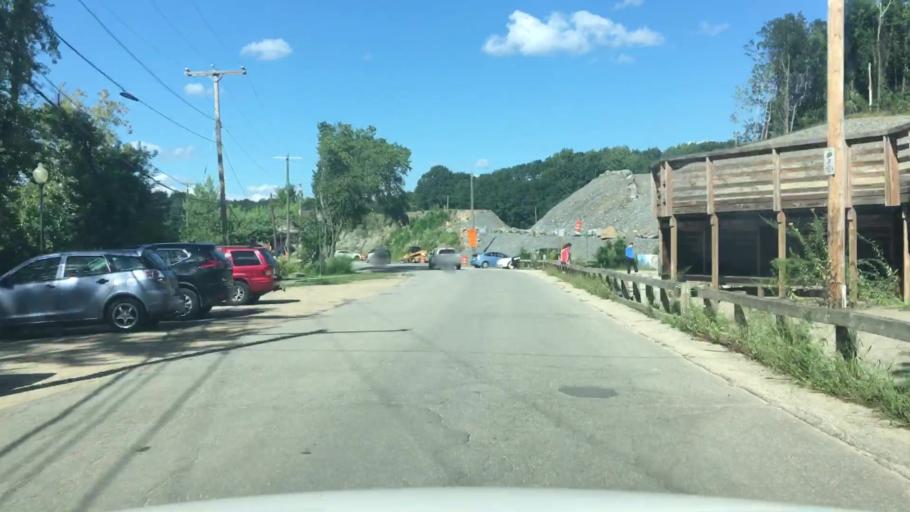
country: US
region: New Hampshire
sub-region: Strafford County
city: Dover
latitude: 43.1937
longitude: -70.8705
